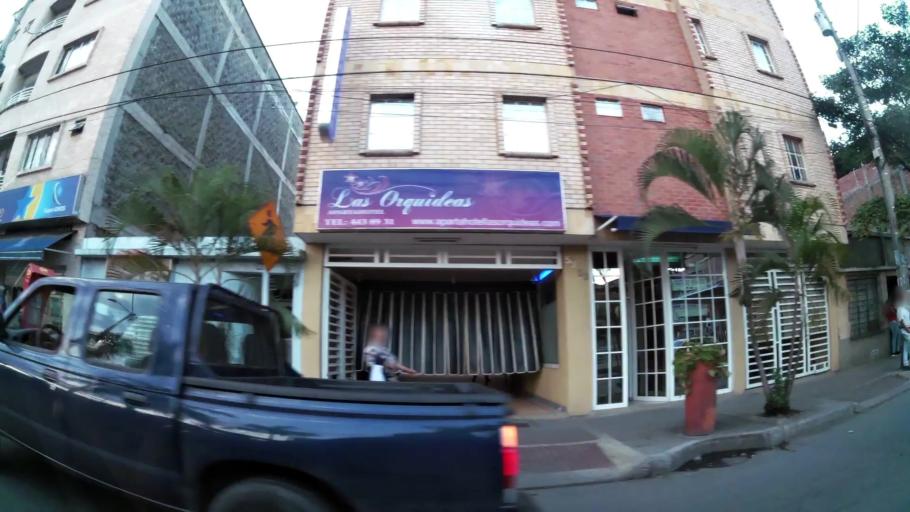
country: CO
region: Valle del Cauca
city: Cali
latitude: 3.4440
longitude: -76.4993
